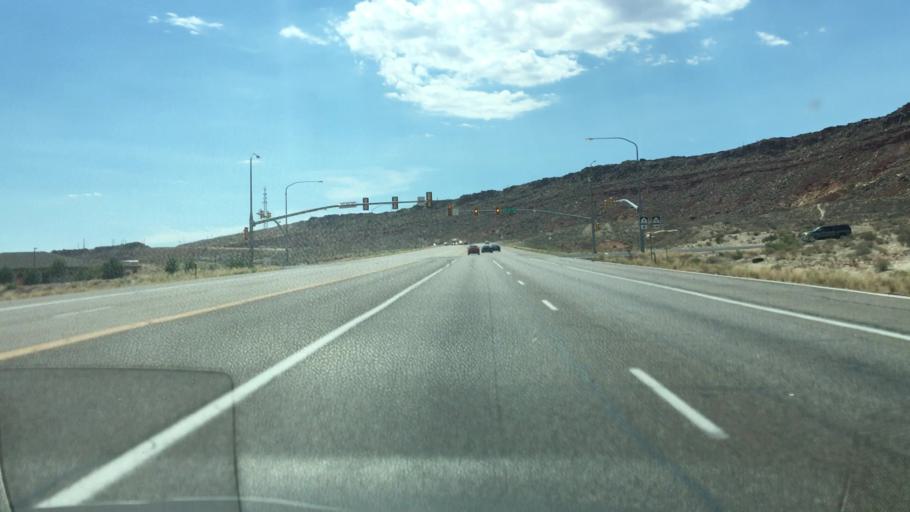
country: US
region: Utah
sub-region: Washington County
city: Washington
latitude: 37.1682
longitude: -113.4066
